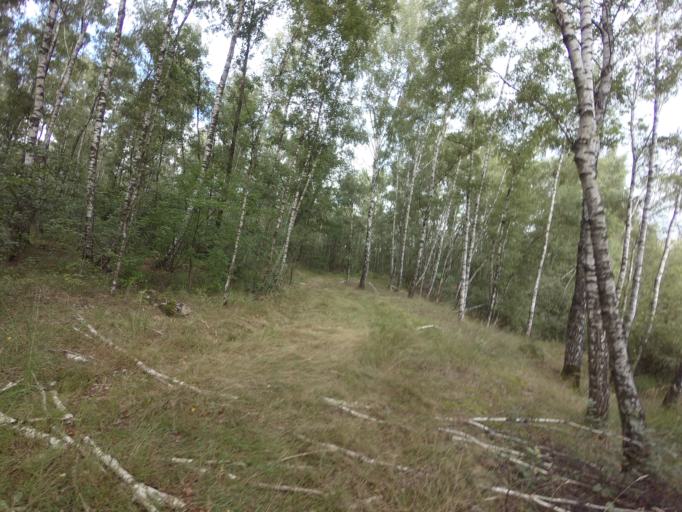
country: NL
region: Limburg
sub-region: Gemeente Onderbanken
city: Schinveld
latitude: 50.9449
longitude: 6.0192
